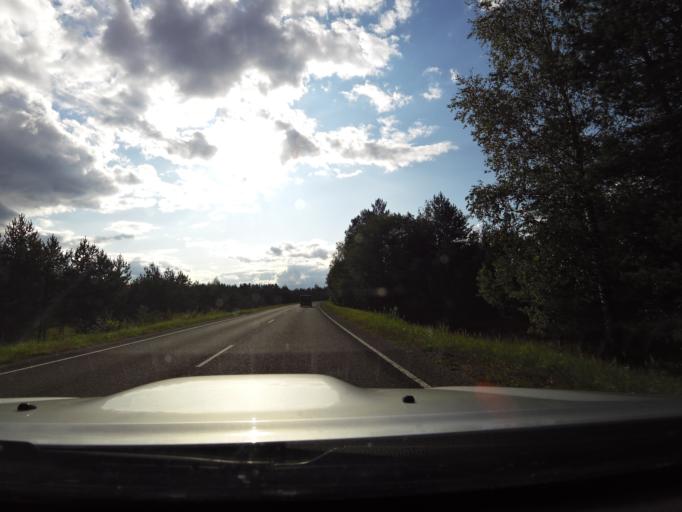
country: LT
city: Juodupe
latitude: 56.2000
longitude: 25.5641
